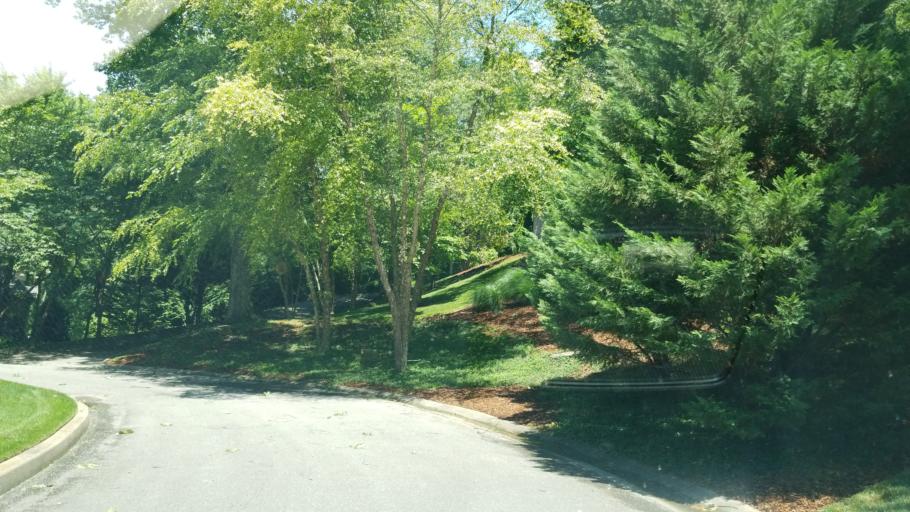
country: US
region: Tennessee
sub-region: Williamson County
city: Brentwood
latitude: 36.0527
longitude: -86.8080
